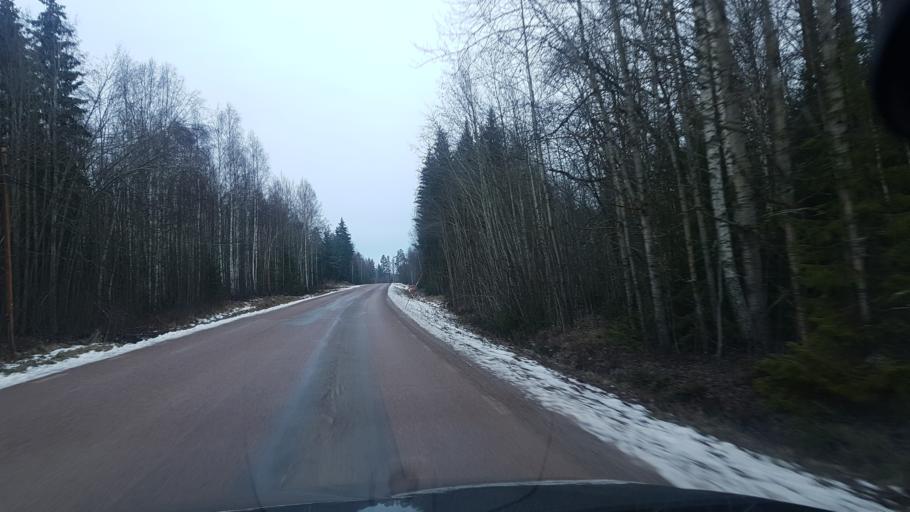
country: SE
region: Dalarna
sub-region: Borlange Kommun
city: Ornas
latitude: 60.4611
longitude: 15.6151
